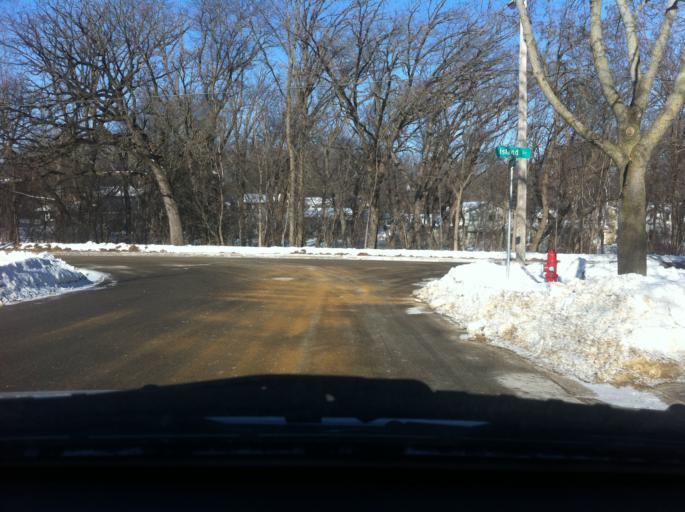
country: US
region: Wisconsin
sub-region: Dane County
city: Middleton
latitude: 43.0633
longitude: -89.4842
